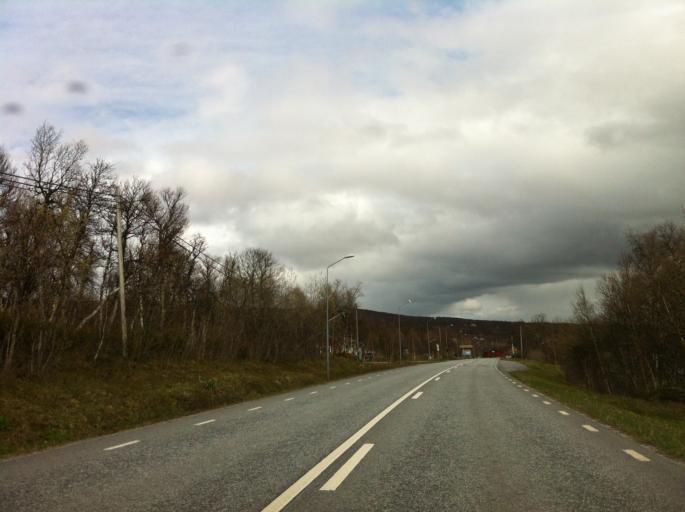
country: NO
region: Sor-Trondelag
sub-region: Tydal
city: Aas
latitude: 62.5512
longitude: 12.2961
